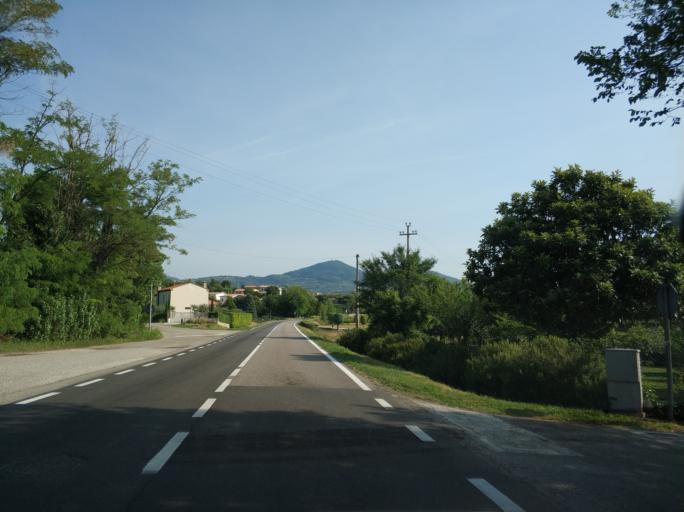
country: IT
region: Veneto
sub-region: Provincia di Padova
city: Arqua Petrarca
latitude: 45.2441
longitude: 11.7116
